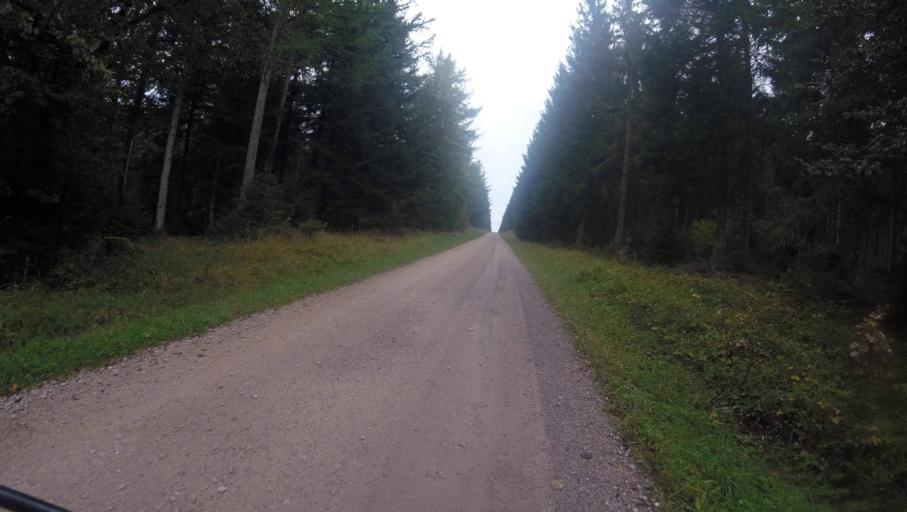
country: DE
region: Baden-Wuerttemberg
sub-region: Karlsruhe Region
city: Loffenau
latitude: 48.7260
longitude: 8.4307
